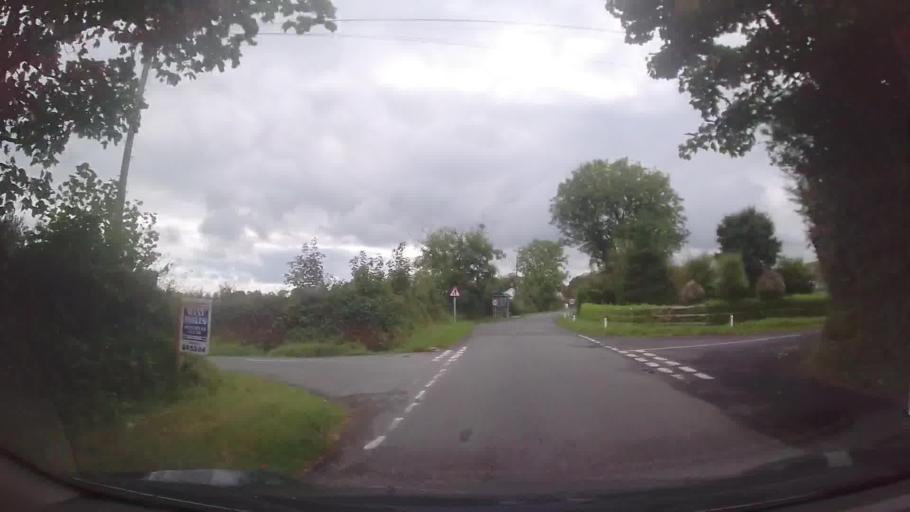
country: GB
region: Wales
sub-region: Carmarthenshire
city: Whitland
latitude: 51.7568
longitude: -4.6404
